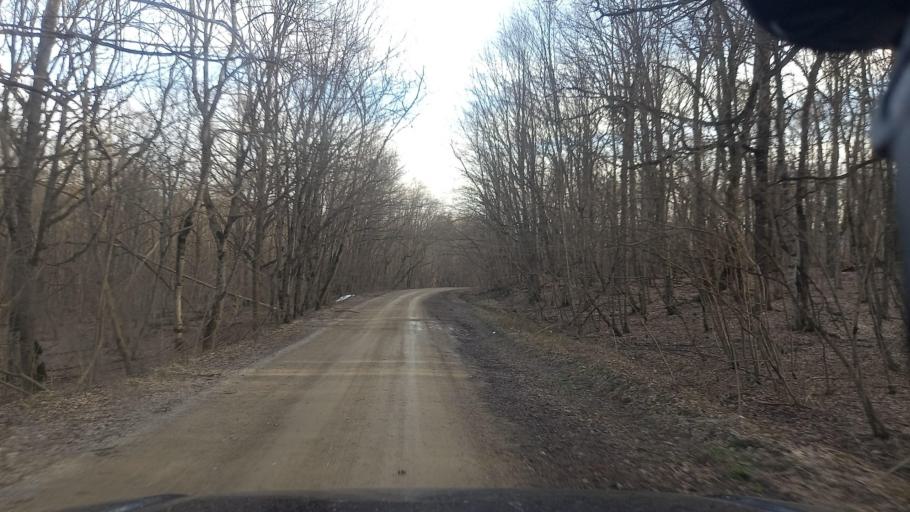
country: RU
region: Krasnodarskiy
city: Novodmitriyevskaya
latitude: 44.6993
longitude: 38.9736
